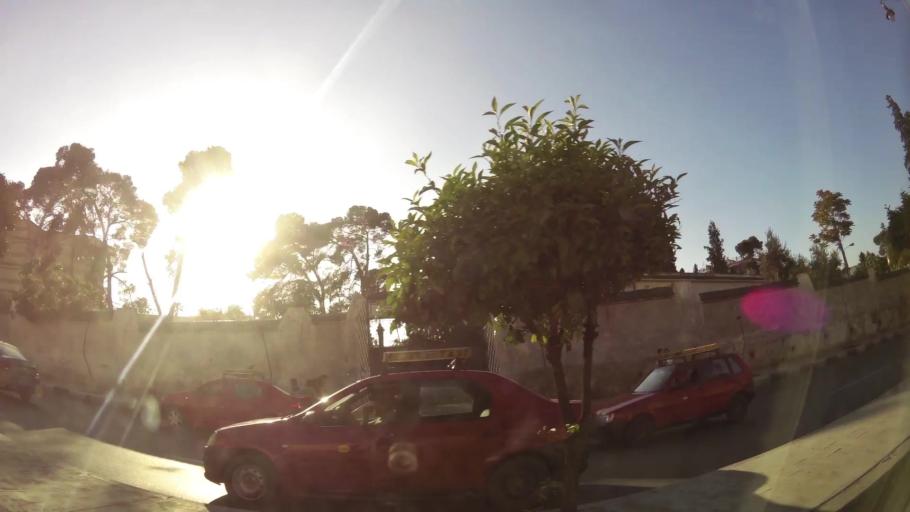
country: MA
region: Fes-Boulemane
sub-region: Fes
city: Fes
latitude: 34.0464
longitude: -4.9953
